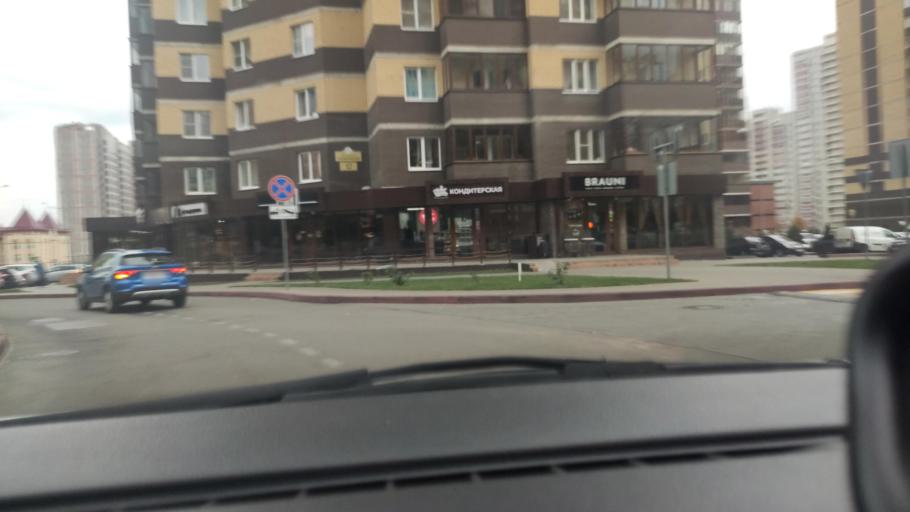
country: RU
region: Voronezj
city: Voronezh
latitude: 51.7148
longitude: 39.1961
